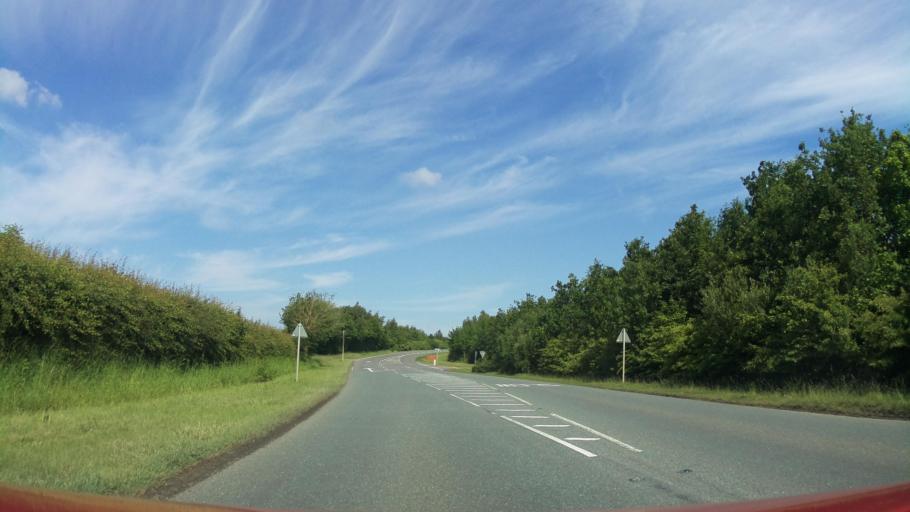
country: GB
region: England
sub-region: Lincolnshire
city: Skellingthorpe
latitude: 53.1659
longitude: -0.6403
